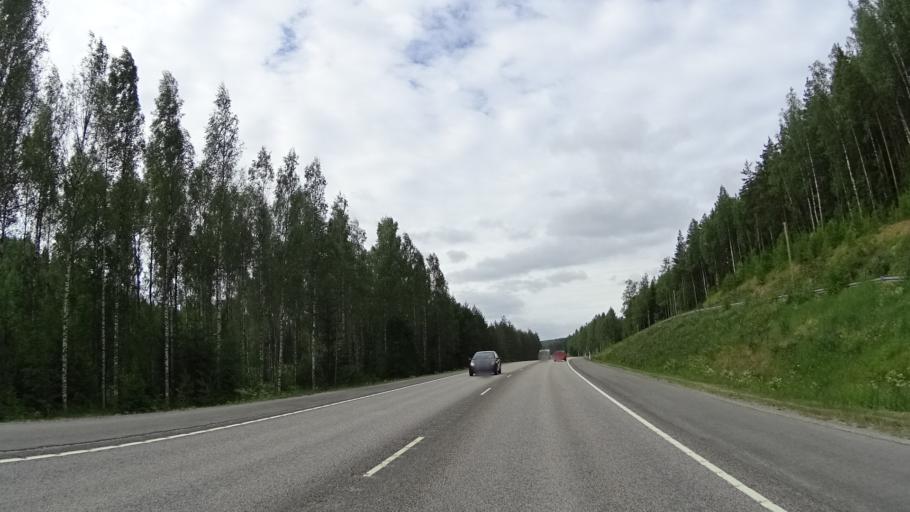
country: FI
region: Uusimaa
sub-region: Helsinki
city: Vihti
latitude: 60.3928
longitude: 24.3262
